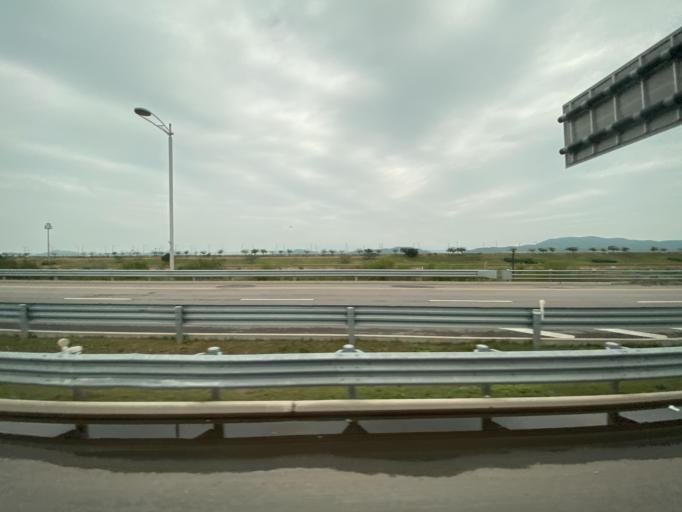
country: KR
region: Incheon
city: Seonwon
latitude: 37.4952
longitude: 126.4227
